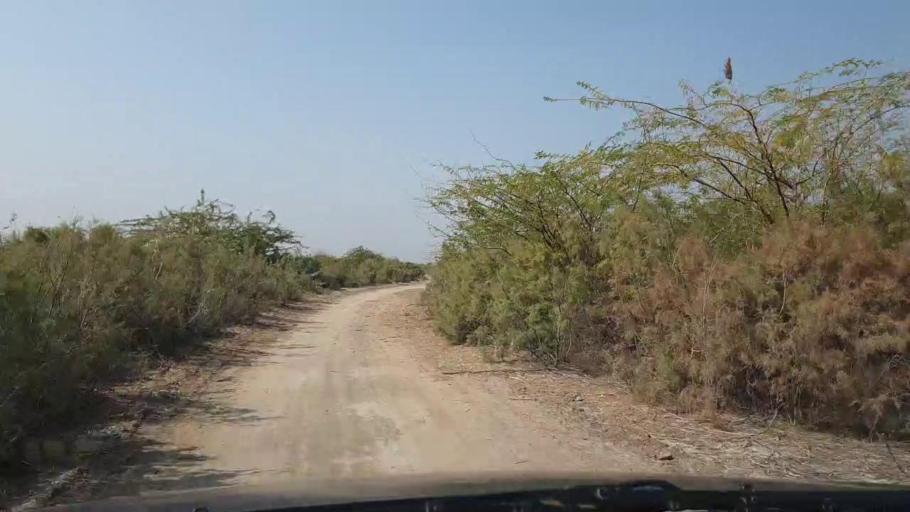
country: PK
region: Sindh
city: Jhol
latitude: 25.8903
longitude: 68.9703
